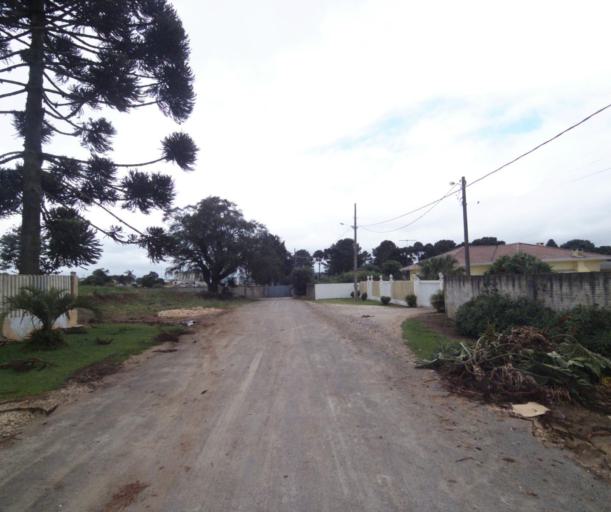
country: BR
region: Parana
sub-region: Quatro Barras
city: Quatro Barras
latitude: -25.3596
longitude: -49.1065
